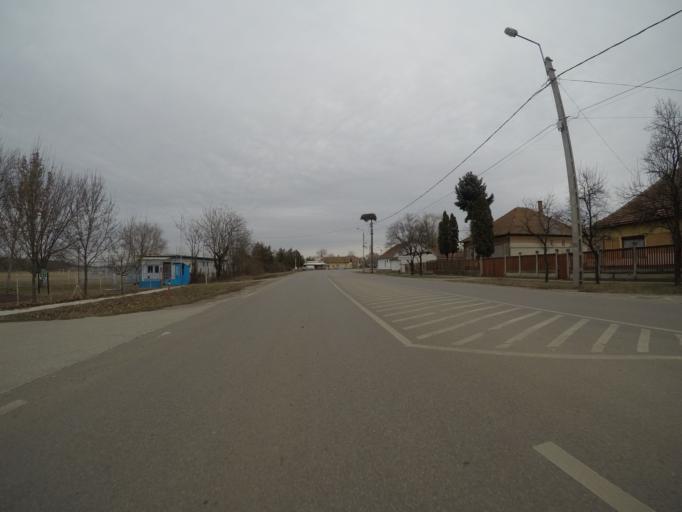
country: HU
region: Jasz-Nagykun-Szolnok
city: Jaszjakohalma
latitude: 47.5224
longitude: 19.9998
